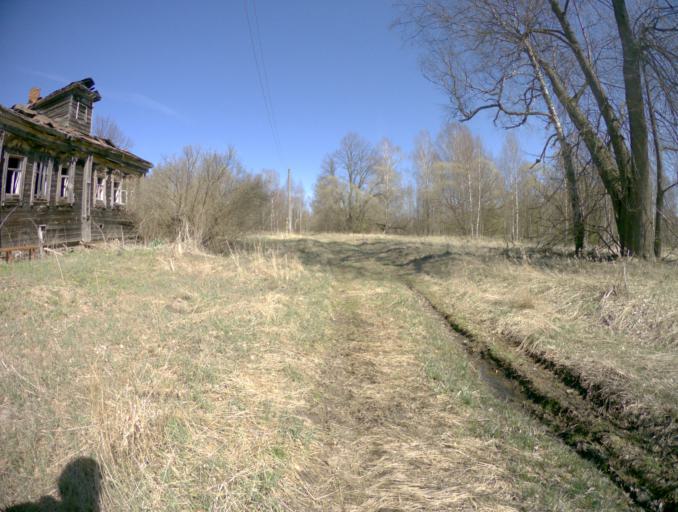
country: RU
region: Vladimir
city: Ivanishchi
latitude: 55.8648
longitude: 40.4362
